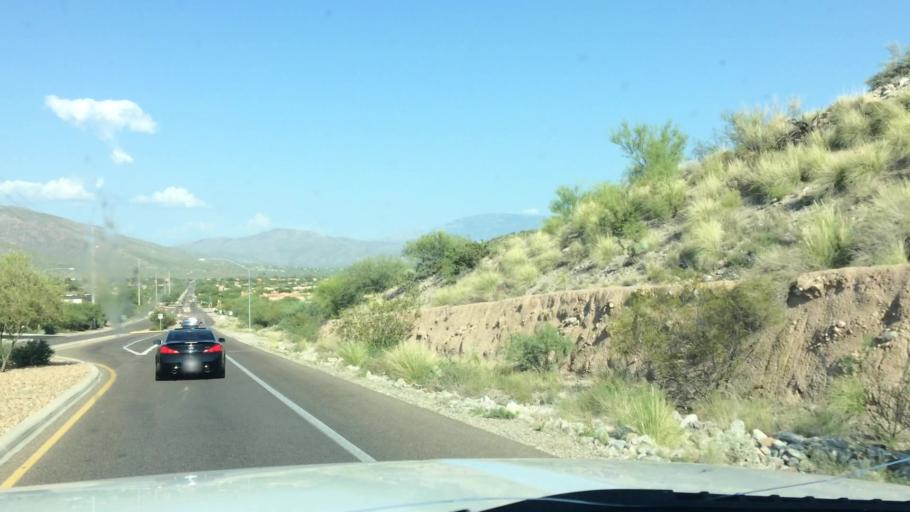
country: US
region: Arizona
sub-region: Pima County
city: Catalina Foothills
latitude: 32.3088
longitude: -110.8500
